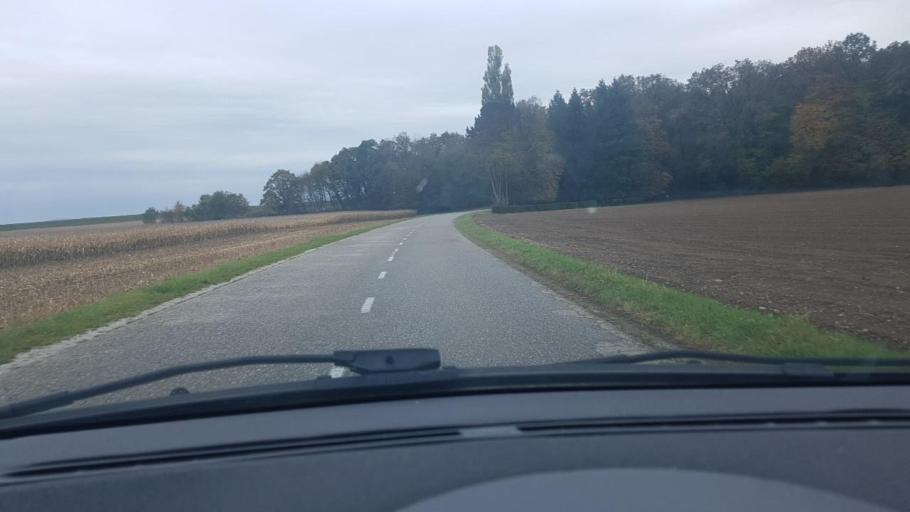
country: SI
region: Starse
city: Starse
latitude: 46.4568
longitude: 15.7649
